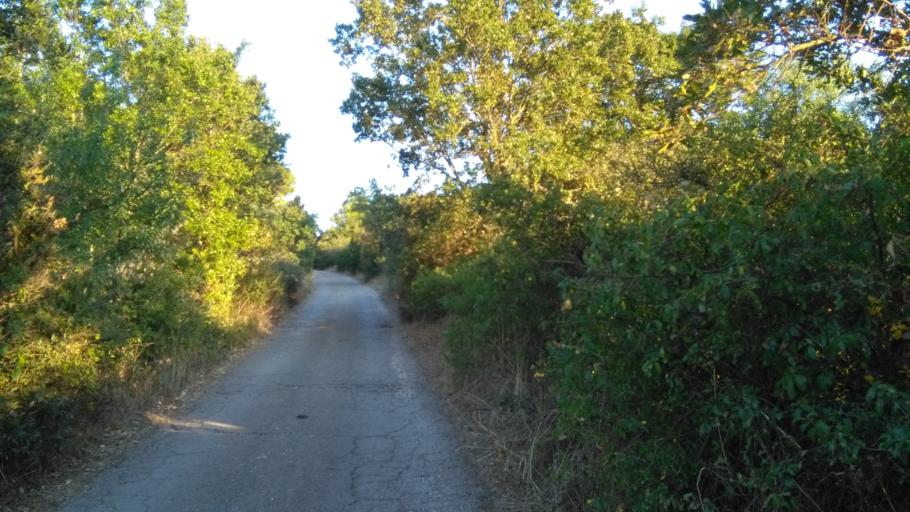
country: IT
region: Apulia
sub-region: Provincia di Bari
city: Putignano
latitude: 40.8259
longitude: 17.0784
